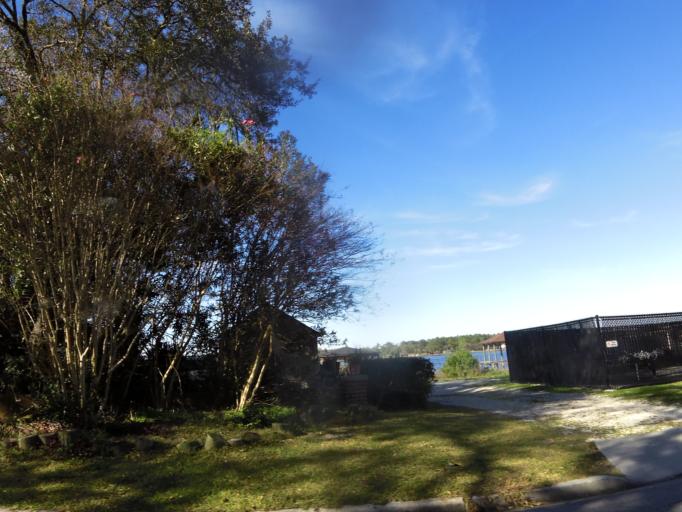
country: US
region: Florida
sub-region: Duval County
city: Jacksonville
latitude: 30.3888
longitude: -81.6549
